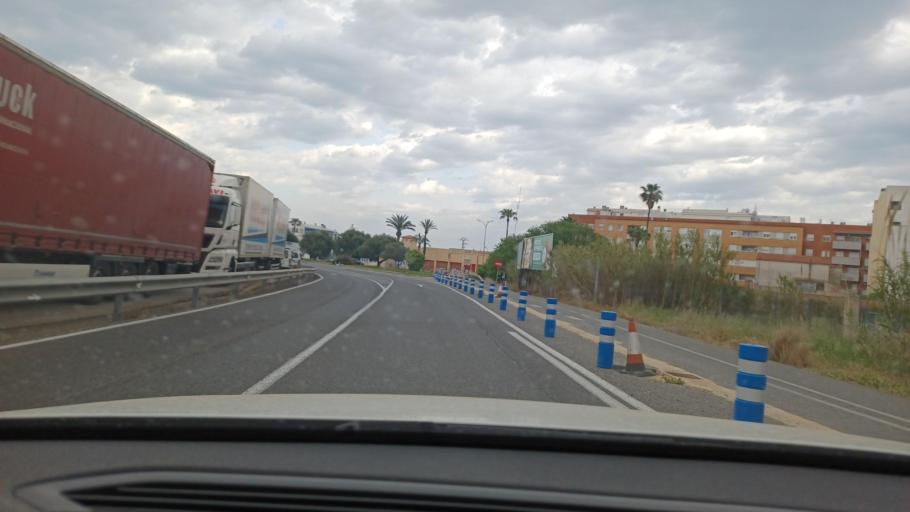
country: ES
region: Valencia
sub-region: Provincia de Castello
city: Benicarlo
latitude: 40.4236
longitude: 0.4278
